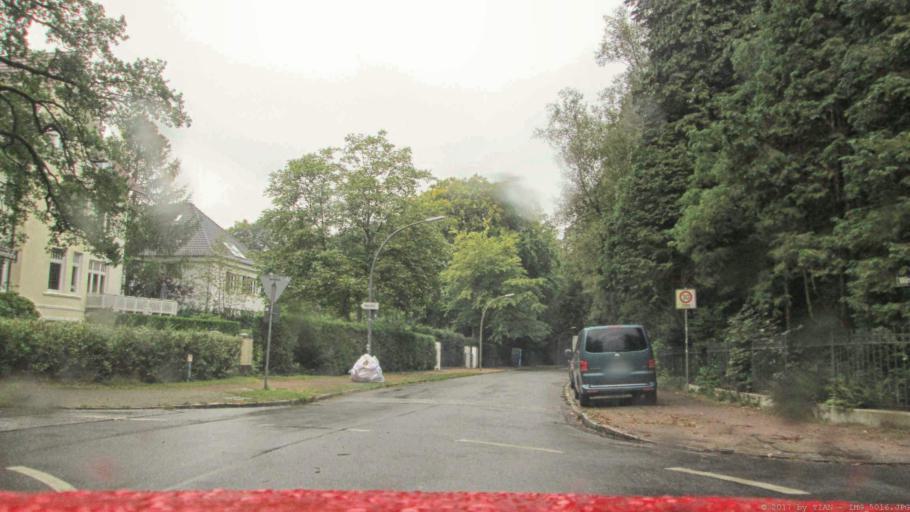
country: DE
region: Schleswig-Holstein
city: Halstenbek
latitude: 53.5596
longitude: 9.8420
